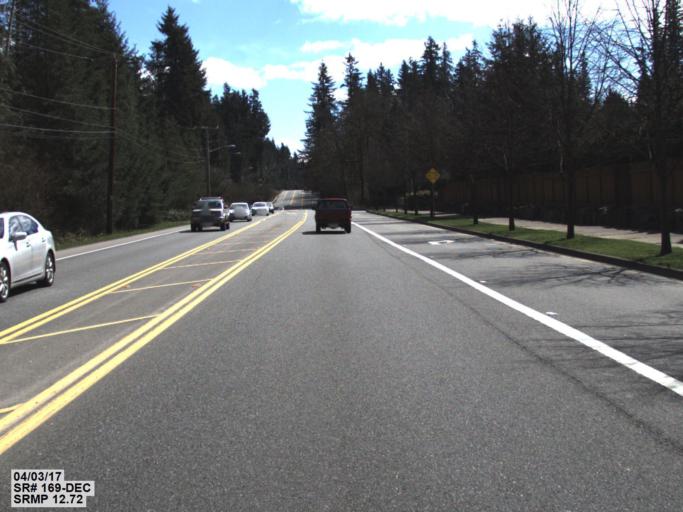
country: US
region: Washington
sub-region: King County
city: Maple Valley
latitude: 47.3791
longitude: -122.0281
